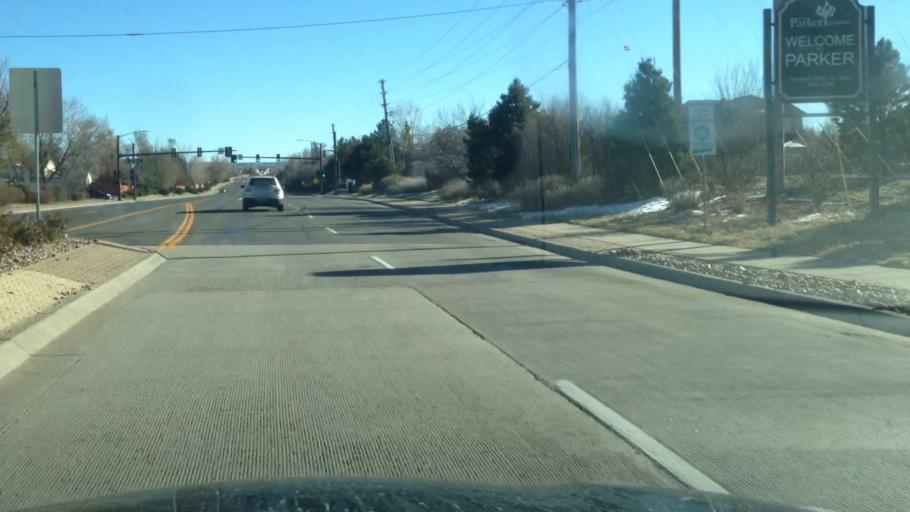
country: US
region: Colorado
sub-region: Arapahoe County
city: Dove Valley
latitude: 39.5660
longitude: -104.8014
